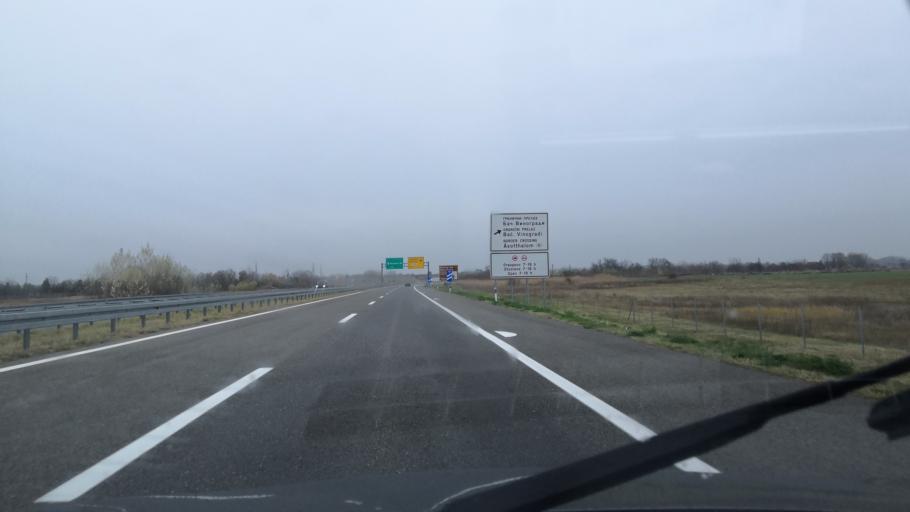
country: HU
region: Csongrad
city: Asotthalom
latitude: 46.1003
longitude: 19.7925
